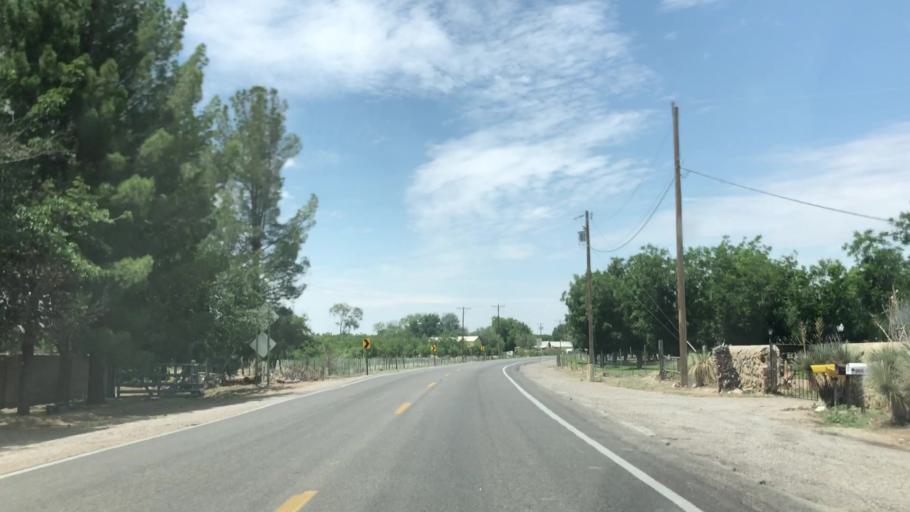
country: US
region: New Mexico
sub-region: Dona Ana County
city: Vado
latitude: 32.1120
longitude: -106.6721
